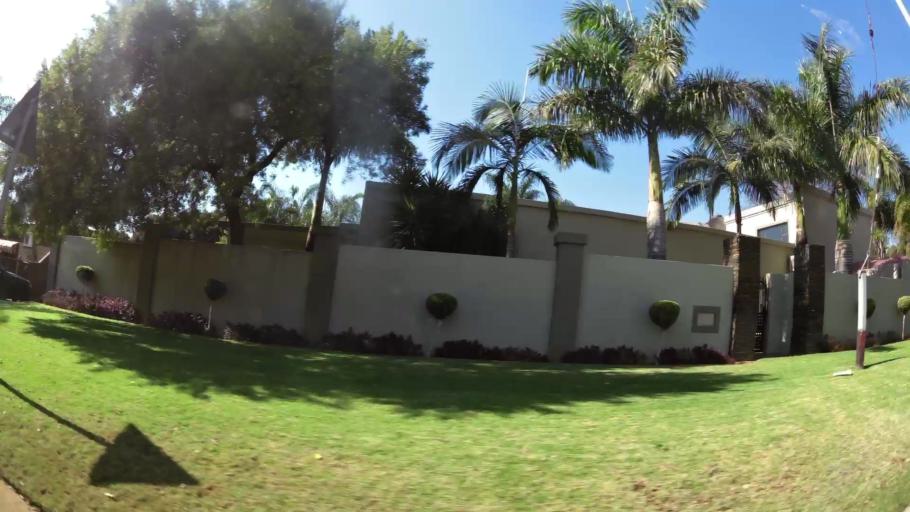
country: ZA
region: Gauteng
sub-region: City of Tshwane Metropolitan Municipality
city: Pretoria
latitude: -25.6839
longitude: 28.2228
